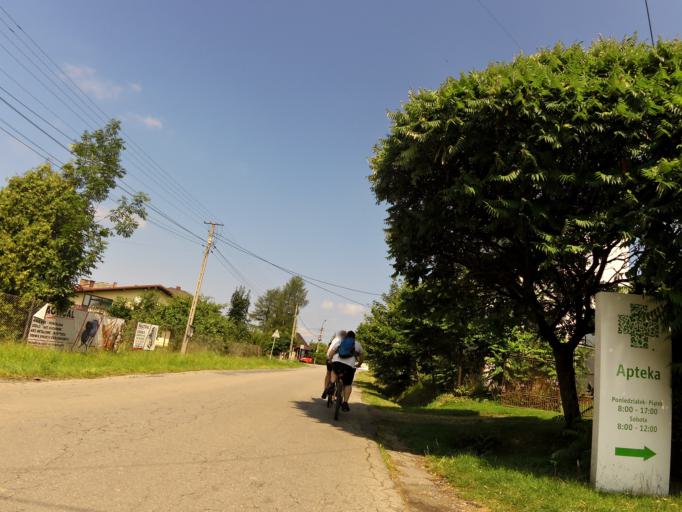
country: PL
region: Silesian Voivodeship
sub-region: Powiat zywiecki
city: Wieprz
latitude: 49.6263
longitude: 19.1680
